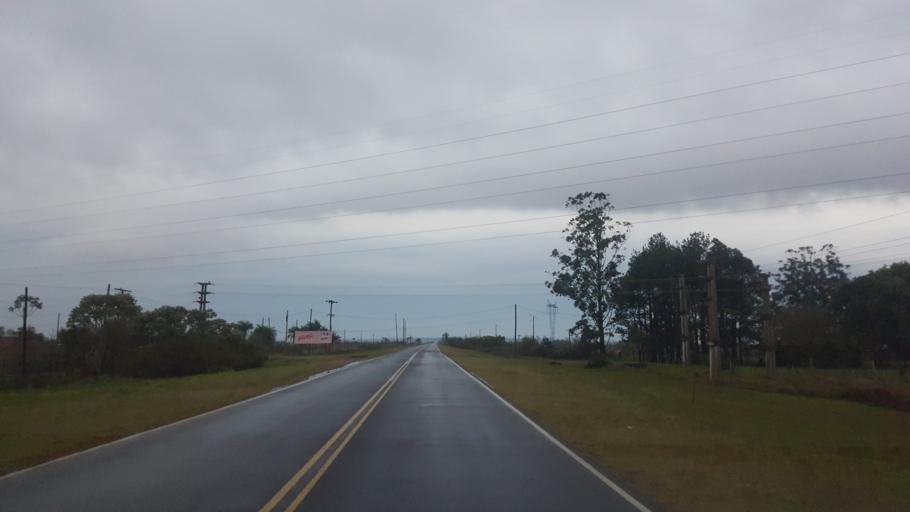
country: AR
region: Corrientes
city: Ituzaingo
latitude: -27.5657
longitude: -56.6618
